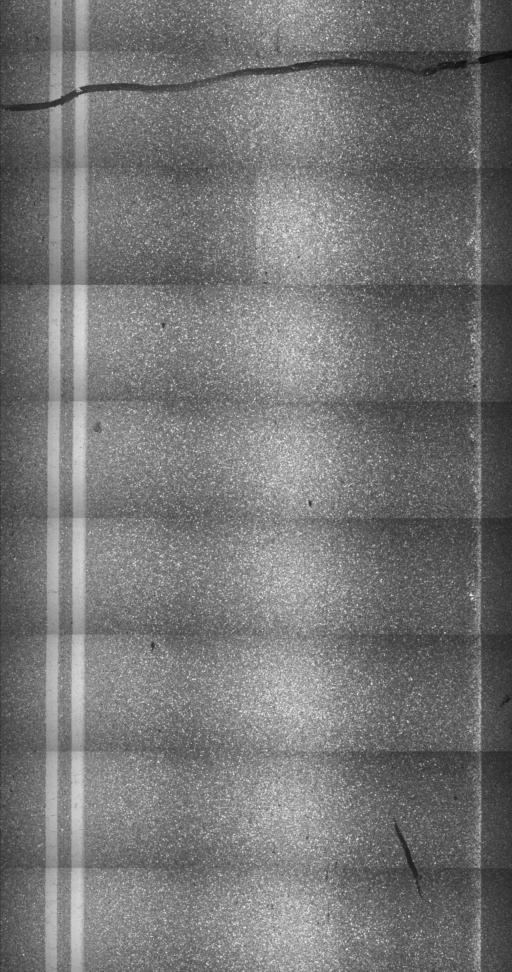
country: US
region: Vermont
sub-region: Washington County
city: Waterbury
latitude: 44.1773
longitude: -72.8350
